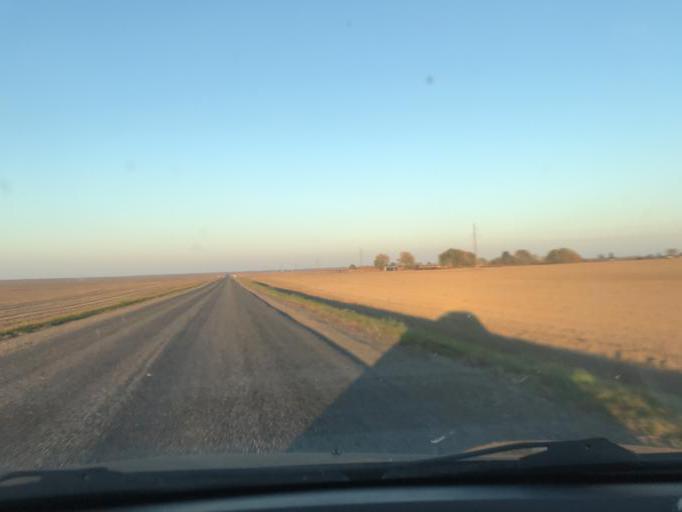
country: BY
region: Gomel
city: Brahin
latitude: 51.8280
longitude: 30.3151
